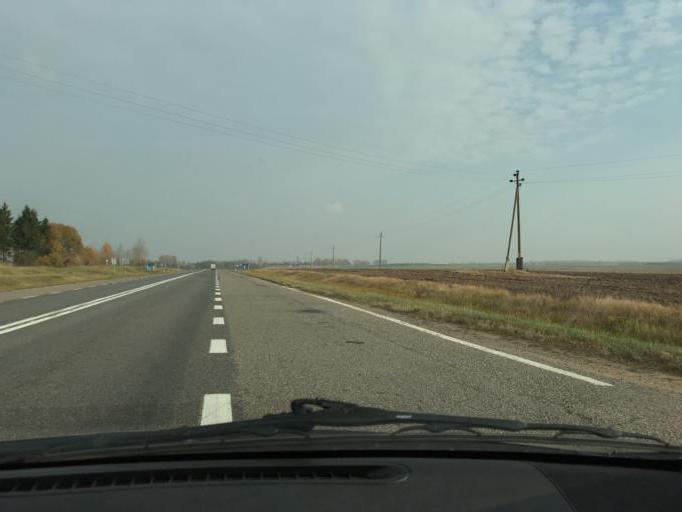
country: BY
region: Vitebsk
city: Chashniki
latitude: 55.0007
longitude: 28.9622
